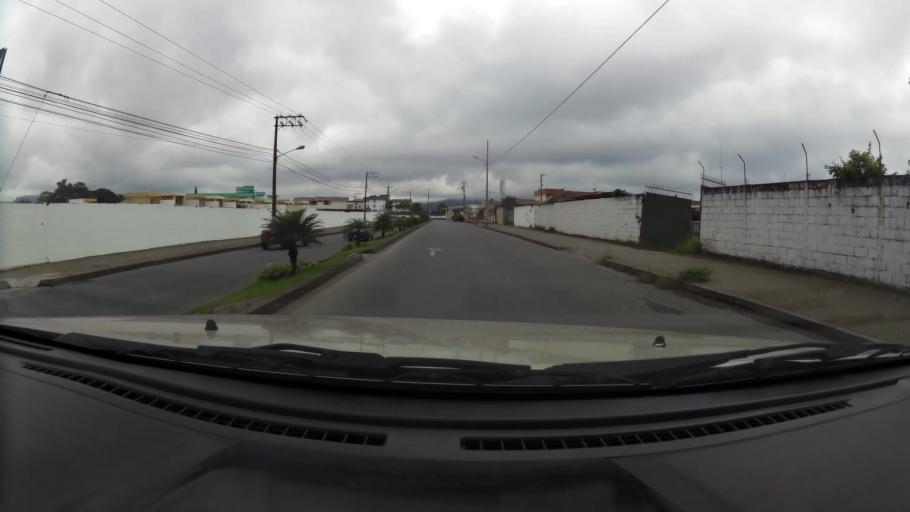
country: EC
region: Santo Domingo de los Tsachilas
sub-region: Canton Santo Domingo de los Colorados
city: Santo Domingo de los Colorados
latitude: -0.2592
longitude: -79.1431
